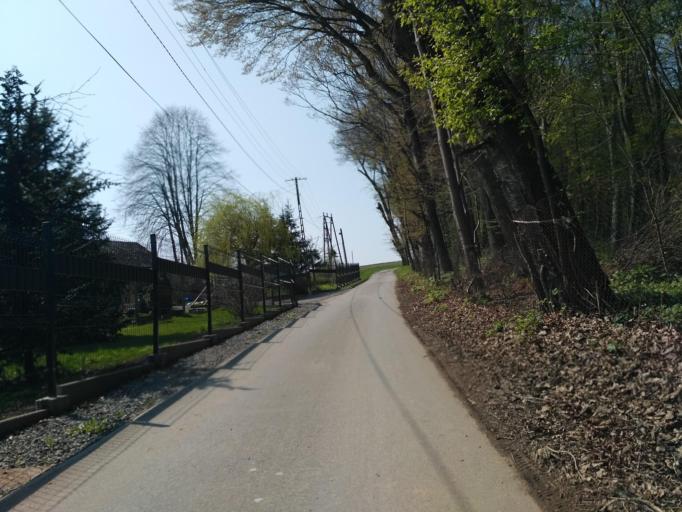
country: PL
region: Subcarpathian Voivodeship
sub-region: Powiat brzozowski
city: Turze Pole
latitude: 49.6432
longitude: 22.0040
